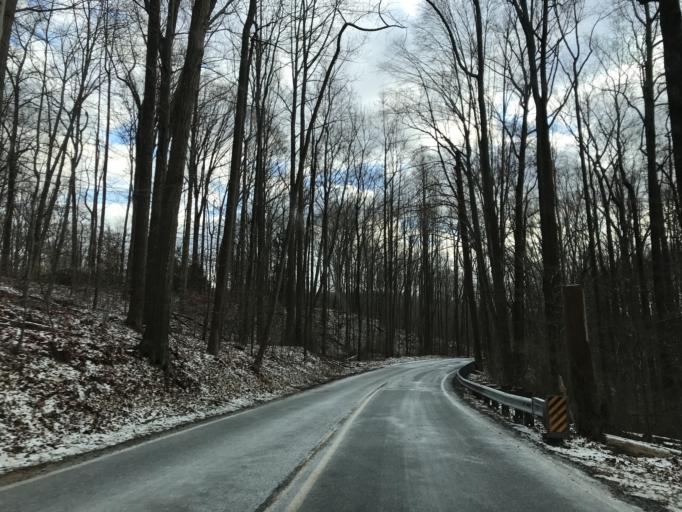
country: US
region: Maryland
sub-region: Harford County
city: Bel Air North
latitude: 39.6330
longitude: -76.3758
